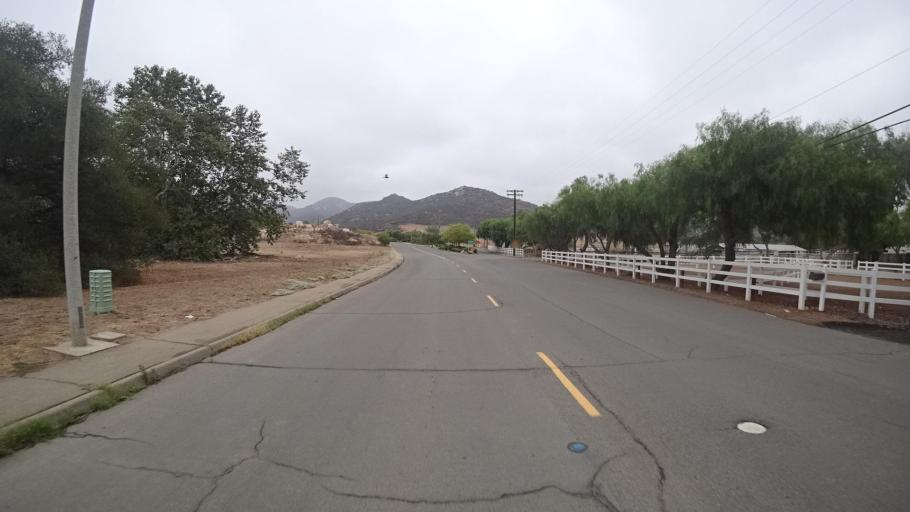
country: US
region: California
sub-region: San Diego County
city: Poway
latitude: 32.9562
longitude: -117.0080
